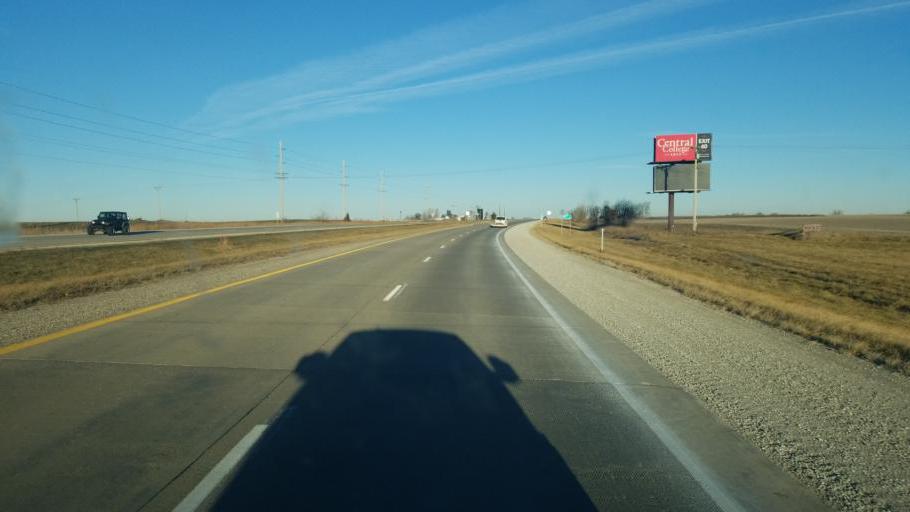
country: US
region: Iowa
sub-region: Marion County
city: Pella
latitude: 41.3783
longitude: -92.8173
